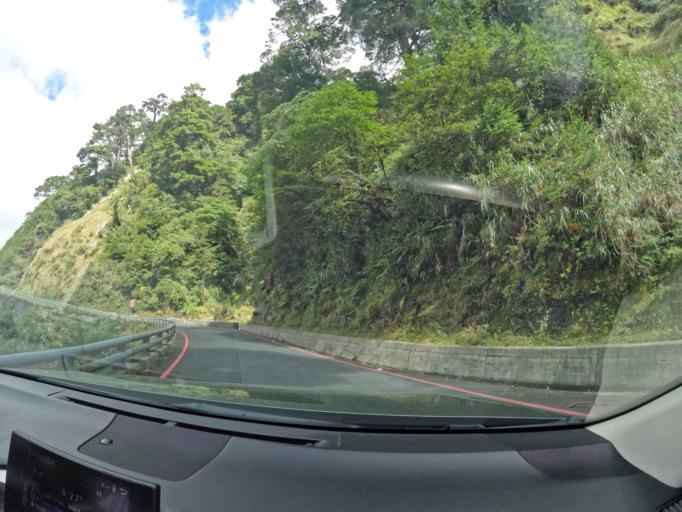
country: TW
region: Taiwan
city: Yujing
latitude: 23.2589
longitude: 120.9456
